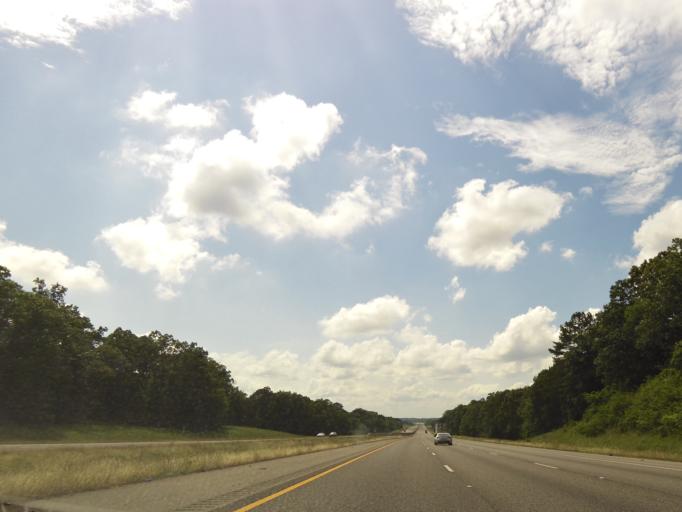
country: US
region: Alabama
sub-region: Calhoun County
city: Bynum
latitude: 33.5777
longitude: -86.0048
